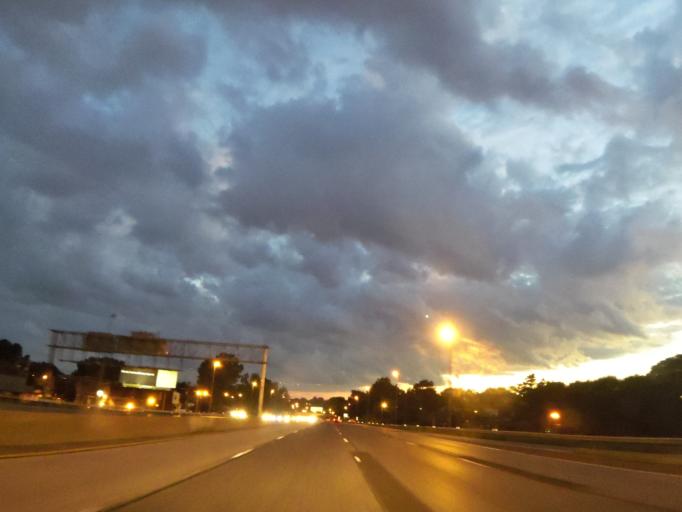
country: US
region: Missouri
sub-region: Saint Louis County
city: Lemay
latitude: 38.5625
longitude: -90.2484
